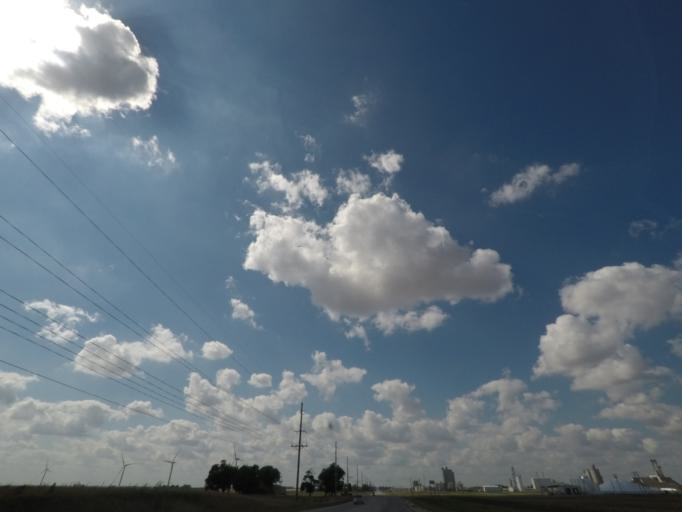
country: US
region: Iowa
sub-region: Story County
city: Nevada
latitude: 42.0231
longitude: -93.4989
